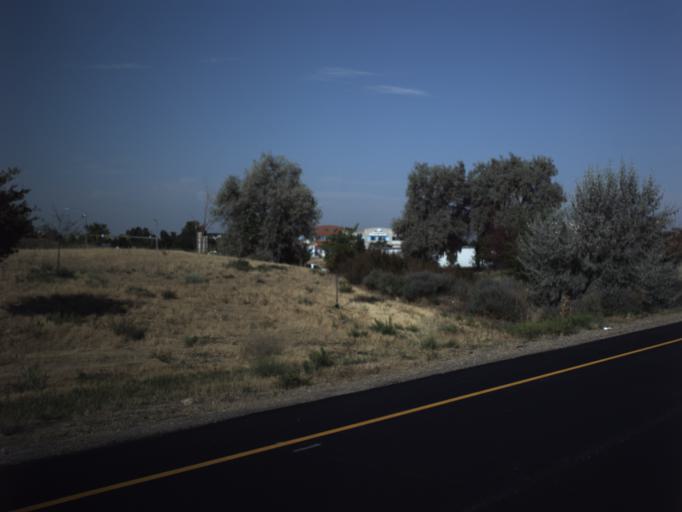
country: US
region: Utah
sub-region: Davis County
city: Hill Air Force Bace
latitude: 41.0902
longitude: -111.9900
